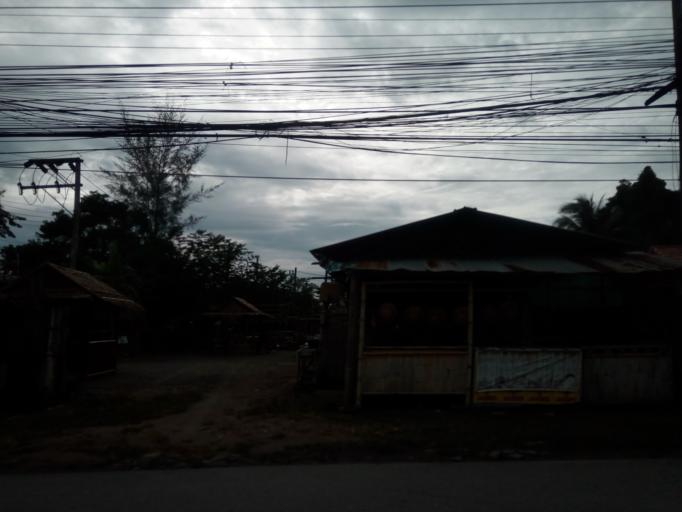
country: TH
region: Phuket
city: Thalang
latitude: 8.0121
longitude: 98.3405
